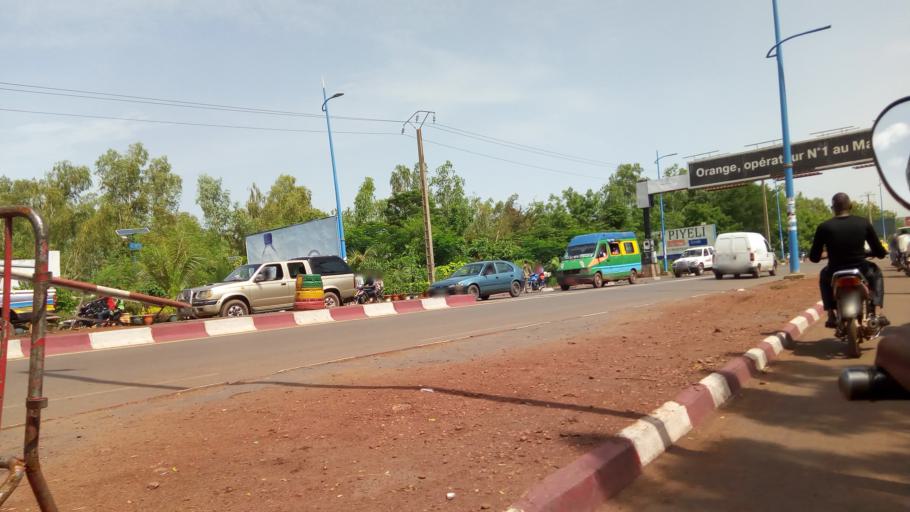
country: ML
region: Bamako
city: Bamako
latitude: 12.6251
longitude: -7.9889
